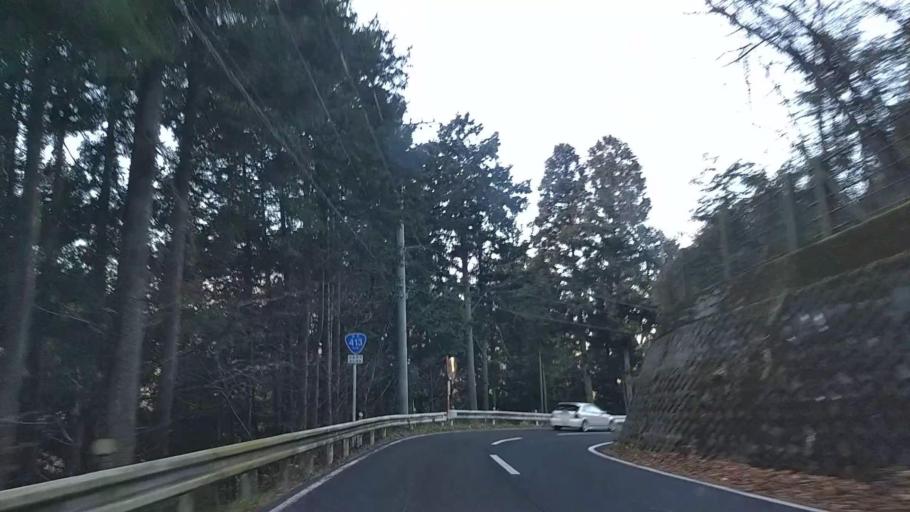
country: JP
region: Yamanashi
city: Uenohara
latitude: 35.5492
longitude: 139.1527
